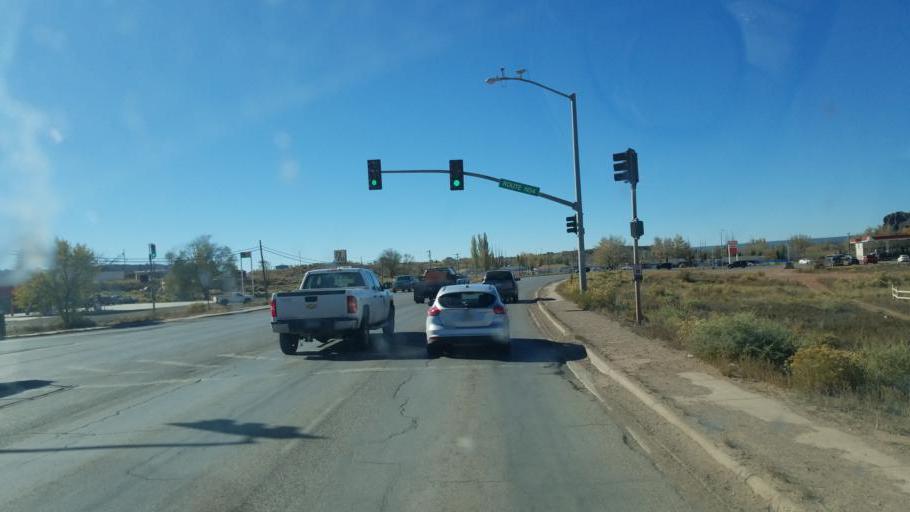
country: US
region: Arizona
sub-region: Apache County
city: Fort Defiance
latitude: 35.7363
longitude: -109.0579
